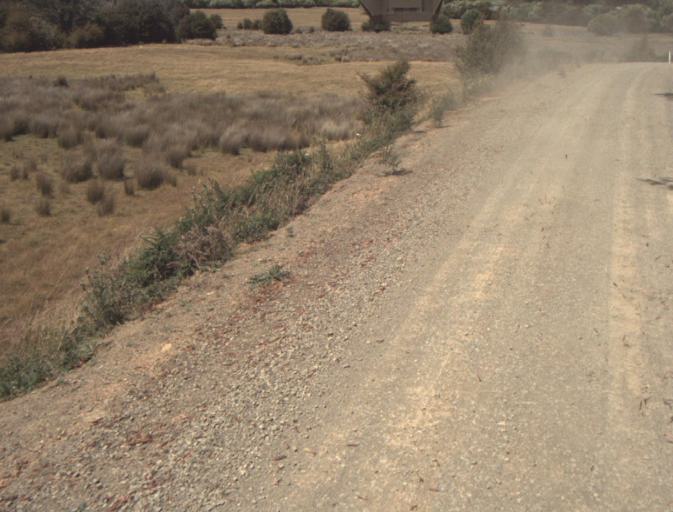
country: AU
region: Tasmania
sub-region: Dorset
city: Scottsdale
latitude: -41.3064
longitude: 147.3687
